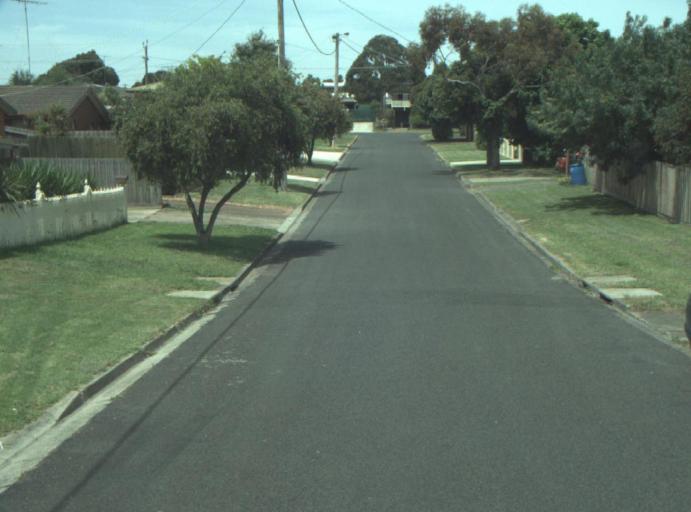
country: AU
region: Victoria
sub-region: Greater Geelong
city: Clifton Springs
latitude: -38.1609
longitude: 144.5634
